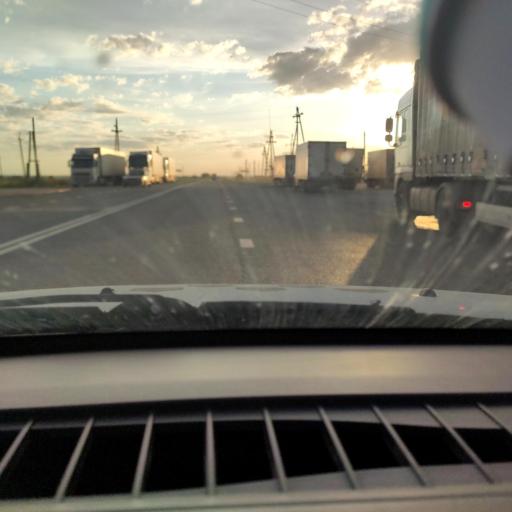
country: RU
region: Kirov
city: Kotel'nich
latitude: 58.3193
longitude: 48.3972
